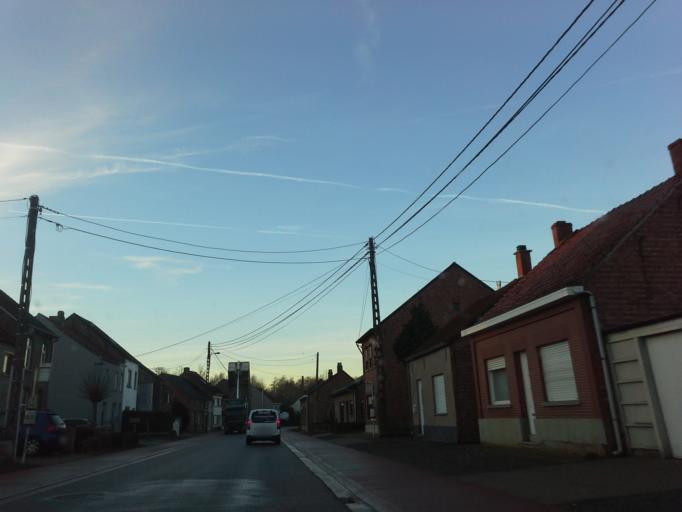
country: BE
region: Flanders
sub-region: Provincie Vlaams-Brabant
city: Scherpenheuvel-Zichem
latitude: 51.0126
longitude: 4.9987
